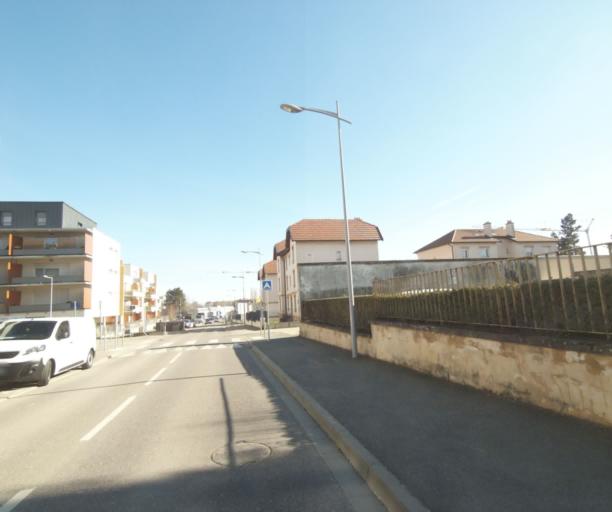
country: FR
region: Lorraine
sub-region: Departement de Meurthe-et-Moselle
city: Nancy
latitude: 48.6695
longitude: 6.1842
